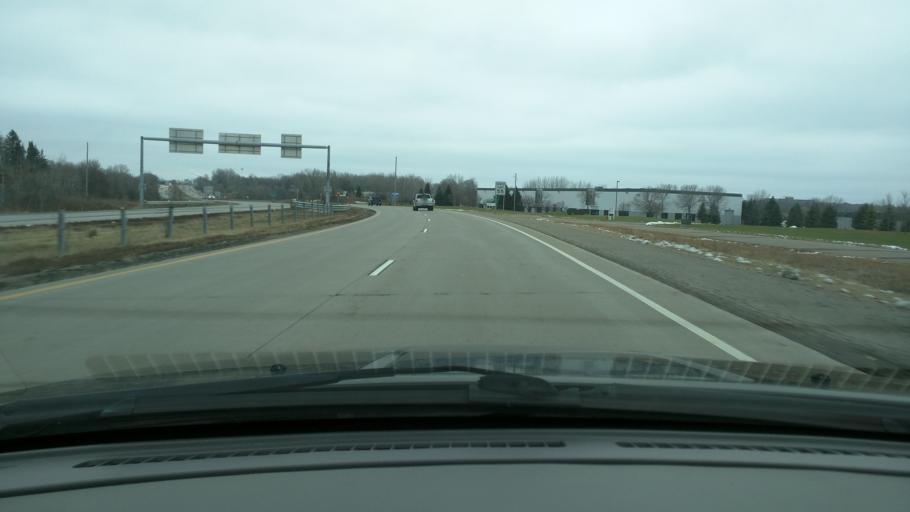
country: US
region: Minnesota
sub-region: Dakota County
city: Mendota Heights
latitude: 44.8733
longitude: -93.1632
